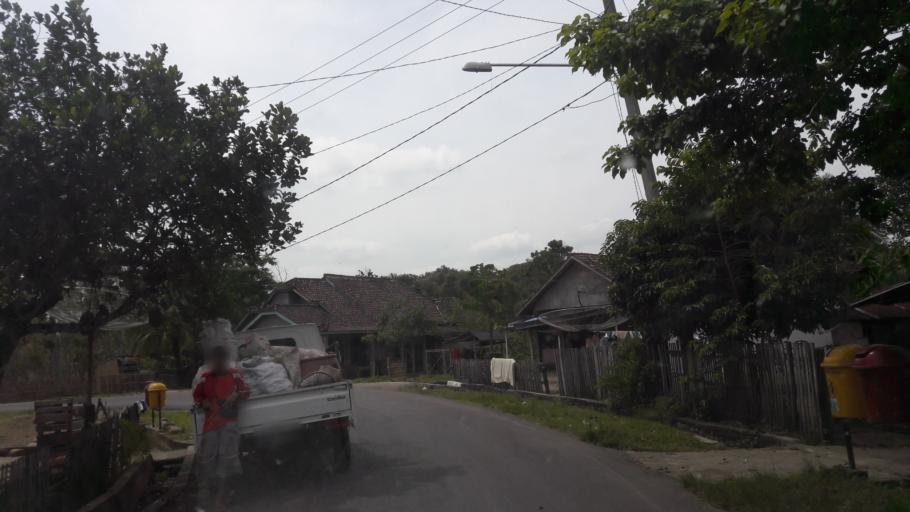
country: ID
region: South Sumatra
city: Gunungmenang
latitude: -3.1103
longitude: 103.9479
